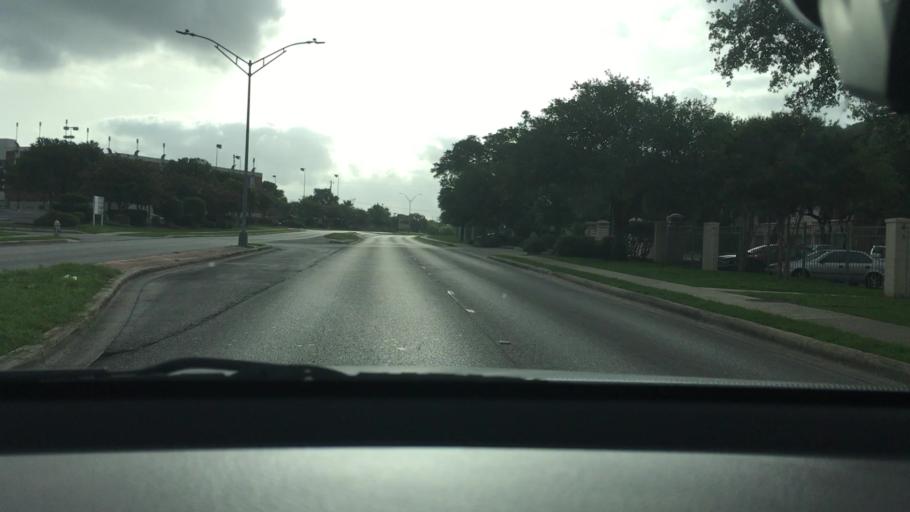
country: US
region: Texas
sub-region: Bexar County
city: Hollywood Park
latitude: 29.6034
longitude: -98.4665
